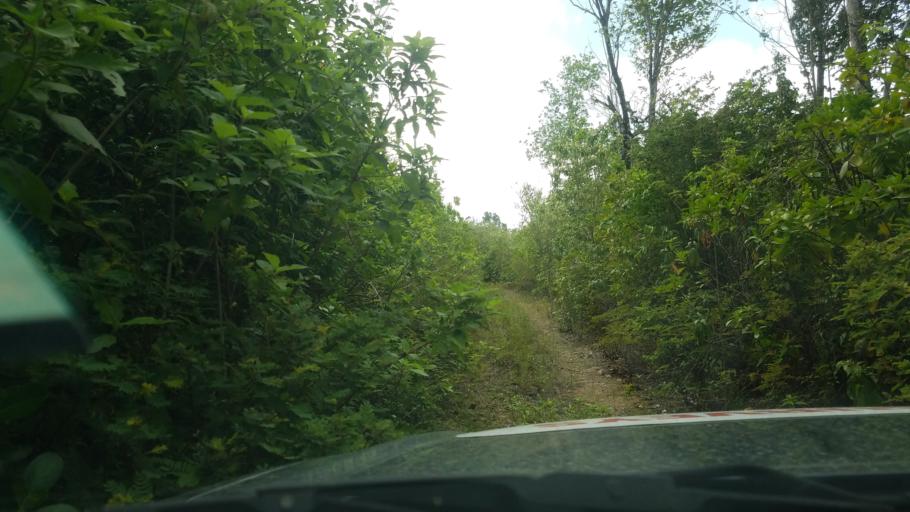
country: LC
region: Anse-la-Raye
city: Anse La Raye
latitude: 13.9440
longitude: -61.0335
